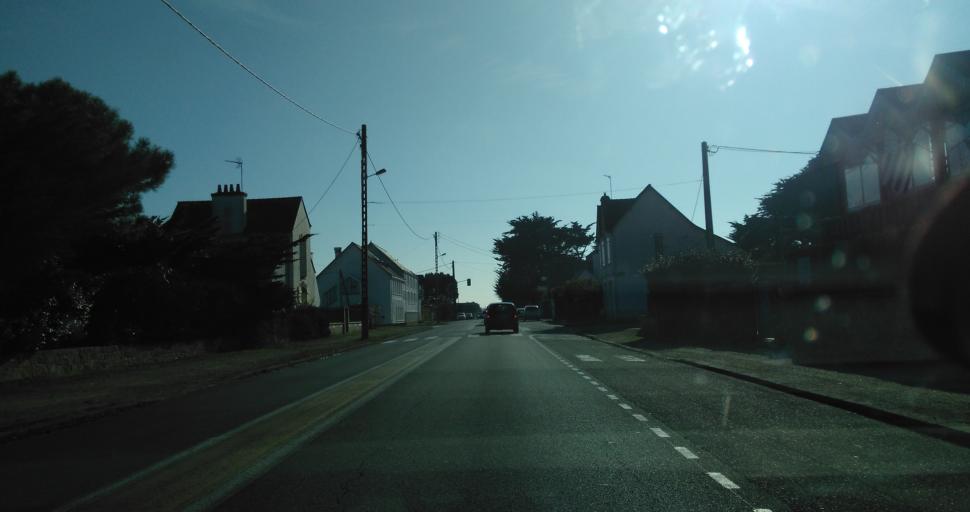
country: FR
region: Brittany
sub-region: Departement du Morbihan
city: Saint-Pierre-Quiberon
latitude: 47.5588
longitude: -3.1344
